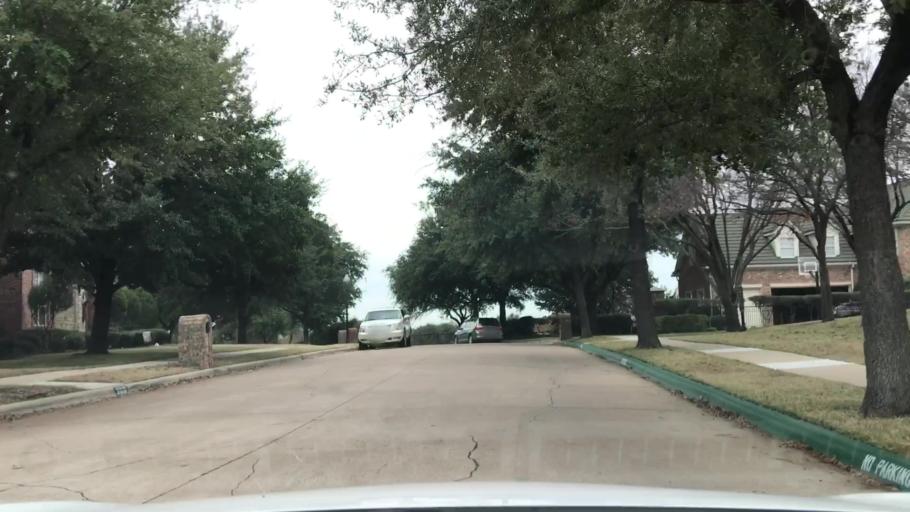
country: US
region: Texas
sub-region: Dallas County
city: Coppell
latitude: 32.9094
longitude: -96.9696
